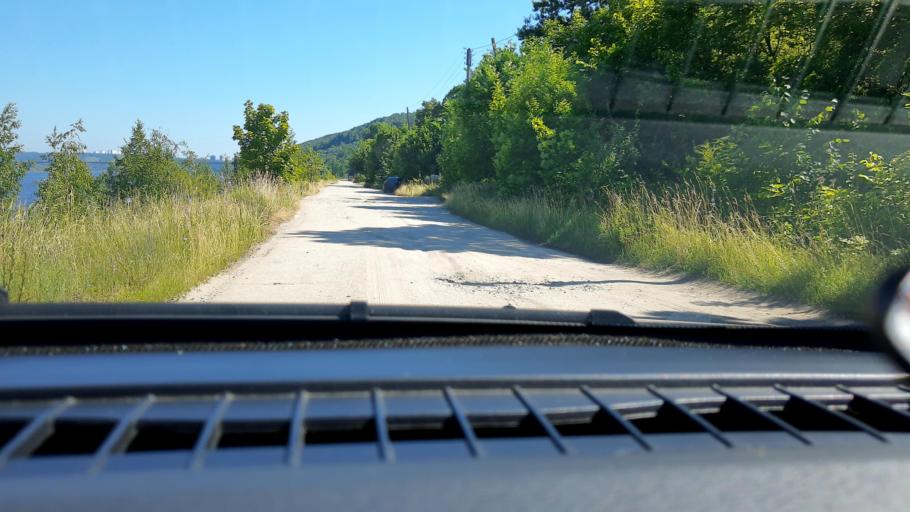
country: RU
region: Nizjnij Novgorod
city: Nizhniy Novgorod
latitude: 56.2299
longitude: 43.9216
